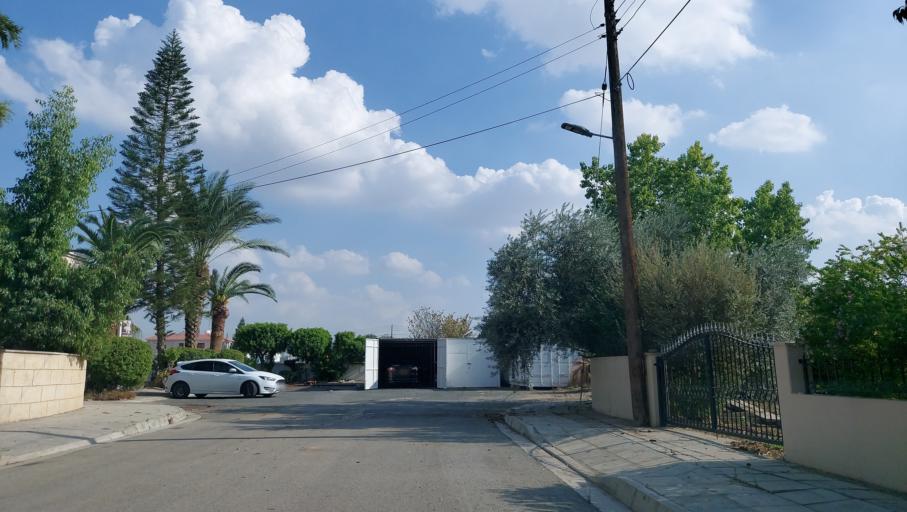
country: CY
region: Lefkosia
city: Tseri
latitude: 35.1025
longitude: 33.3063
